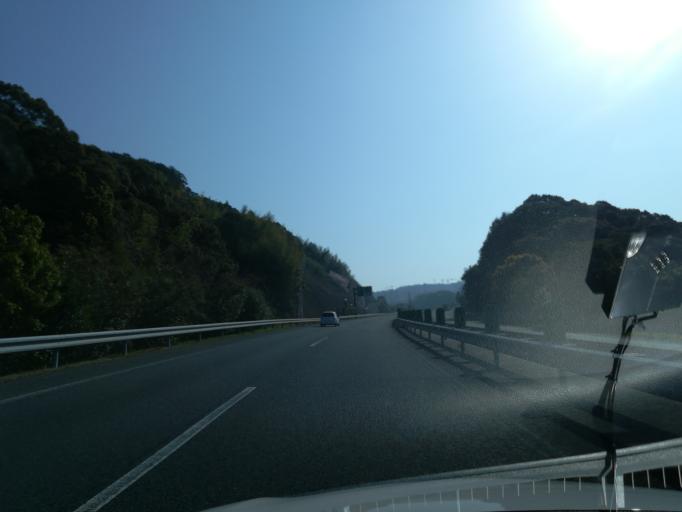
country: JP
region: Kochi
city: Kochi-shi
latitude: 33.6014
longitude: 133.6104
